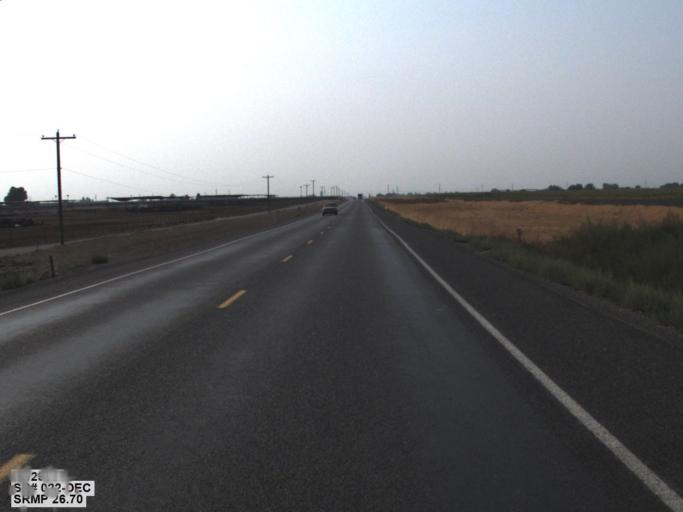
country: US
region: Washington
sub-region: Yakima County
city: Grandview
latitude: 46.1944
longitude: -119.9291
